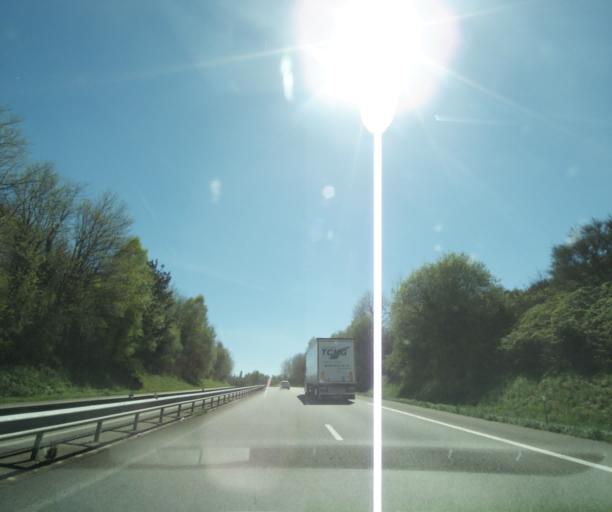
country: FR
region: Limousin
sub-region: Departement de la Haute-Vienne
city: Saint-Germain-les-Belles
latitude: 45.6047
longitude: 1.4471
